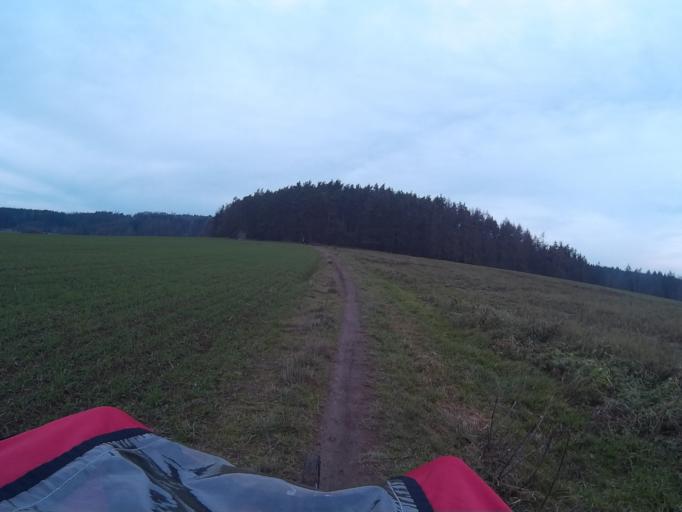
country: CZ
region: Plzensky
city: St'ahlavy
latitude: 49.6799
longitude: 13.4846
